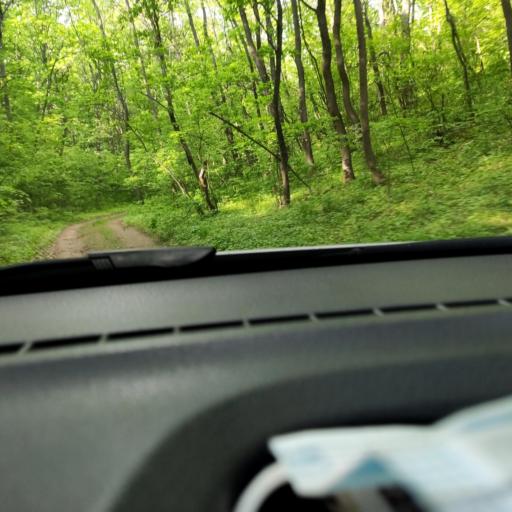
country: RU
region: Voronezj
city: Ramon'
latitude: 51.9410
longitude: 39.3689
